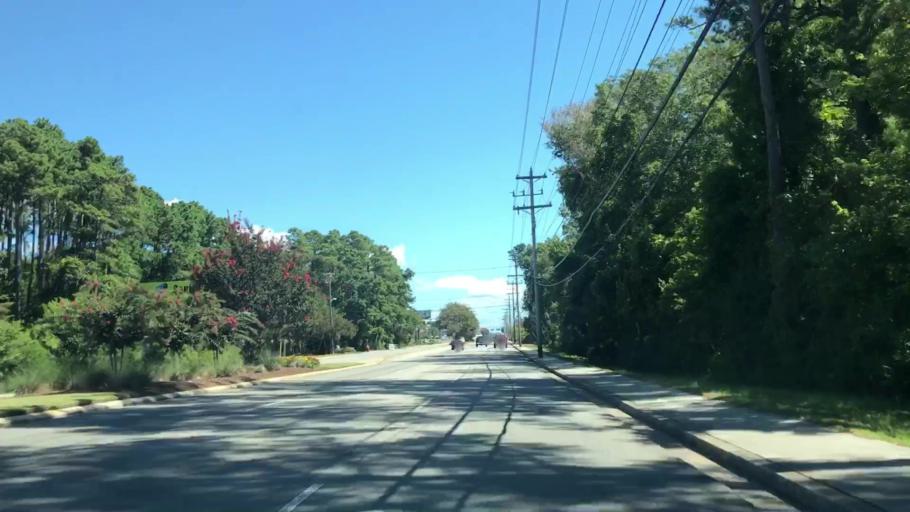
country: US
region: South Carolina
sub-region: Horry County
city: North Myrtle Beach
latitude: 33.8194
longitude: -78.6907
